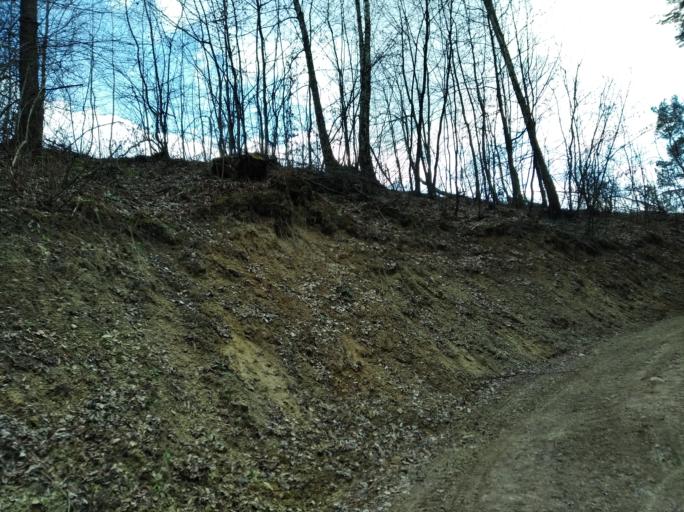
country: PL
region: Subcarpathian Voivodeship
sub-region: Powiat strzyzowski
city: Jawornik
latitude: 49.8457
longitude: 21.8469
